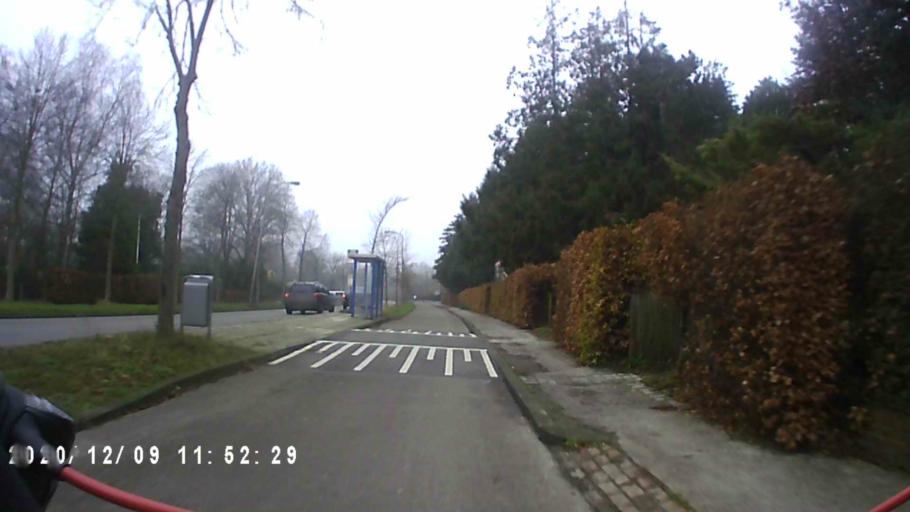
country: NL
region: Groningen
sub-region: Gemeente Haren
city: Haren
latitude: 53.1773
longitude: 6.5994
